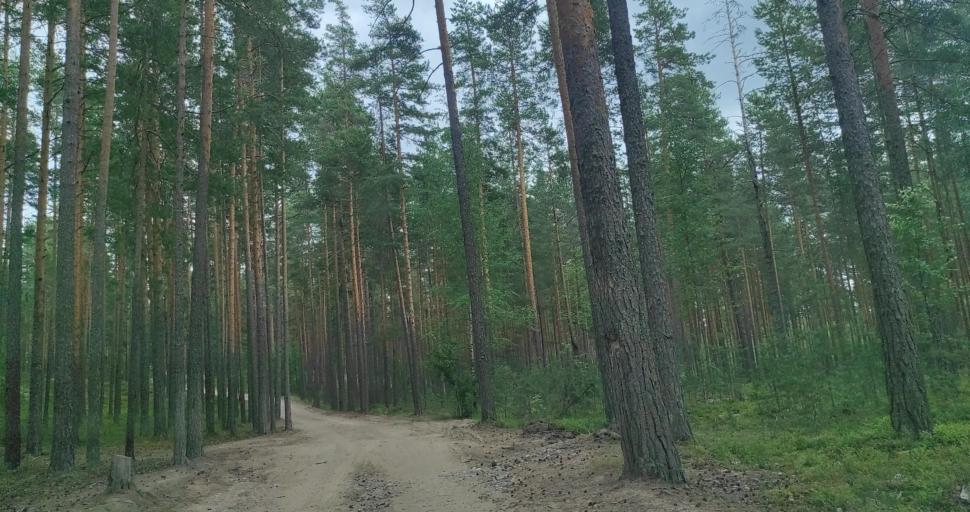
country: RU
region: Leningrad
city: Sapernoye
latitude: 60.6772
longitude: 29.9592
